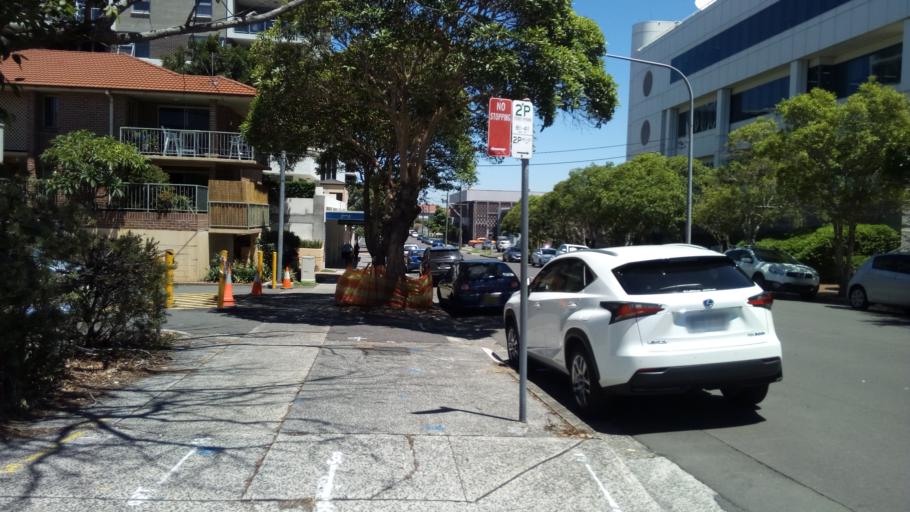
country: AU
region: New South Wales
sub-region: Wollongong
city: Wollongong
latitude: -34.4263
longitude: 150.8909
